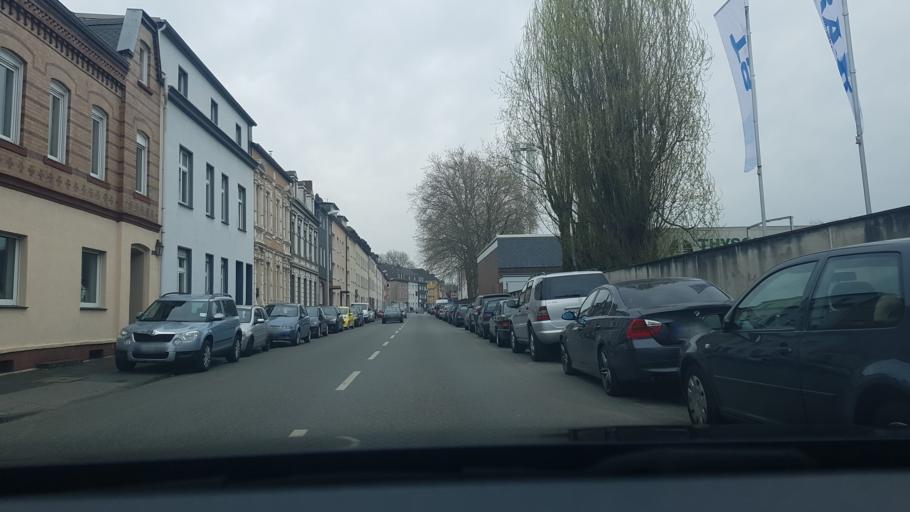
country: DE
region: North Rhine-Westphalia
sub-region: Regierungsbezirk Dusseldorf
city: Muelheim (Ruhr)
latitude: 51.4368
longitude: 6.8783
